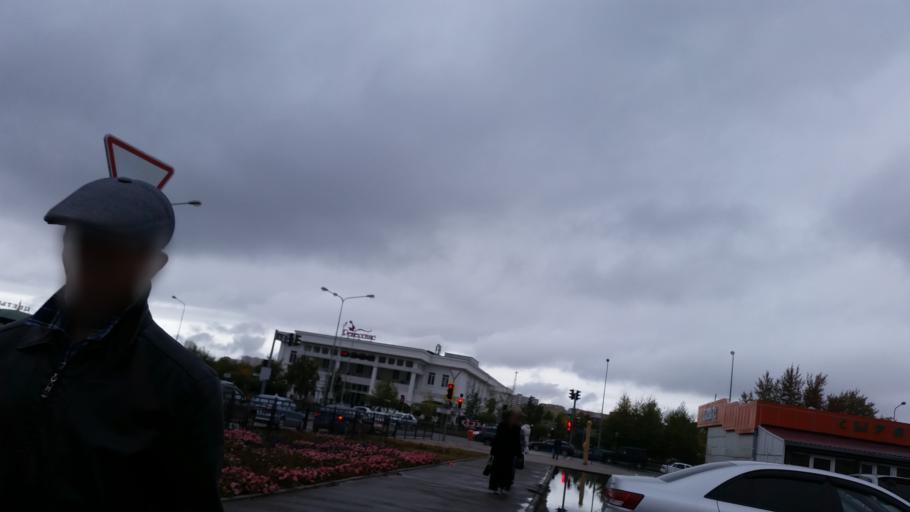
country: KZ
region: Astana Qalasy
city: Astana
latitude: 51.1519
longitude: 71.4617
